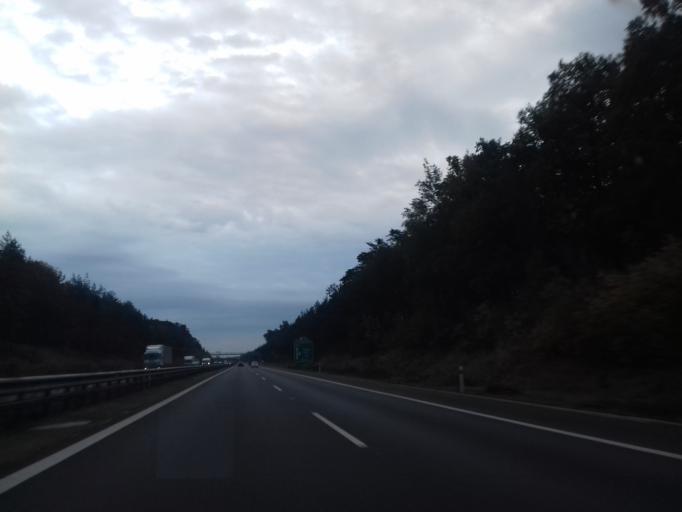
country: CZ
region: Central Bohemia
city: Poricany
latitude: 50.1224
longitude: 14.9308
